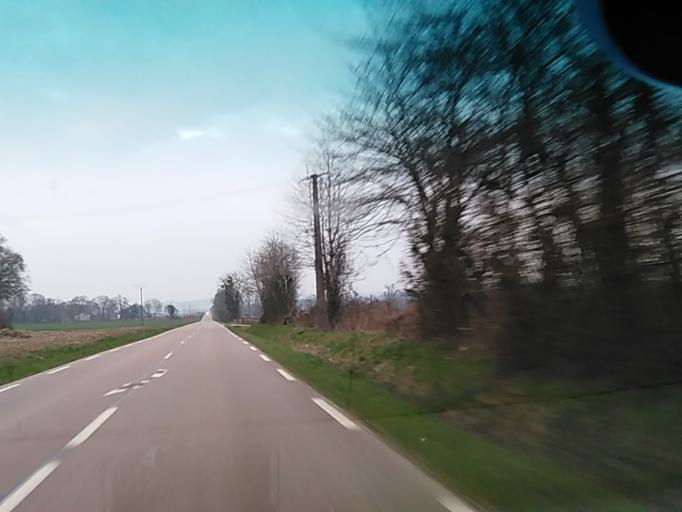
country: FR
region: Lower Normandy
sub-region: Departement de l'Orne
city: Pont-Ecrepin
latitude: 48.7227
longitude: -0.2632
